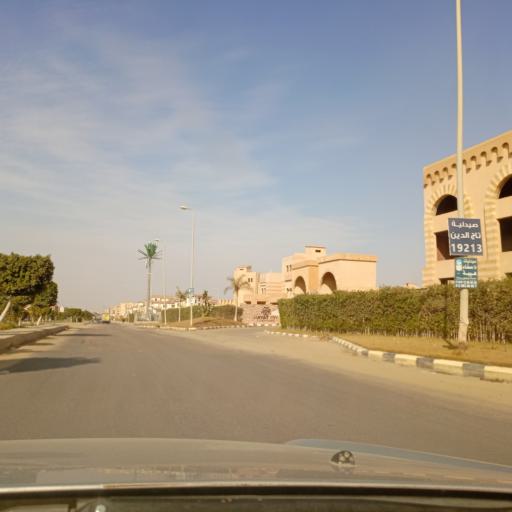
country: EG
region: Muhafazat al Qalyubiyah
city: Al Khankah
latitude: 30.0366
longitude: 31.4852
